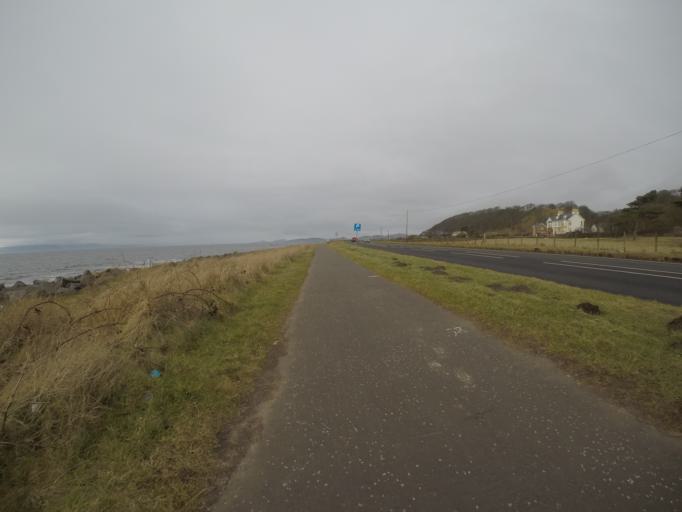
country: GB
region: Scotland
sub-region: North Ayrshire
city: West Kilbride
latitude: 55.6661
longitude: -4.8394
